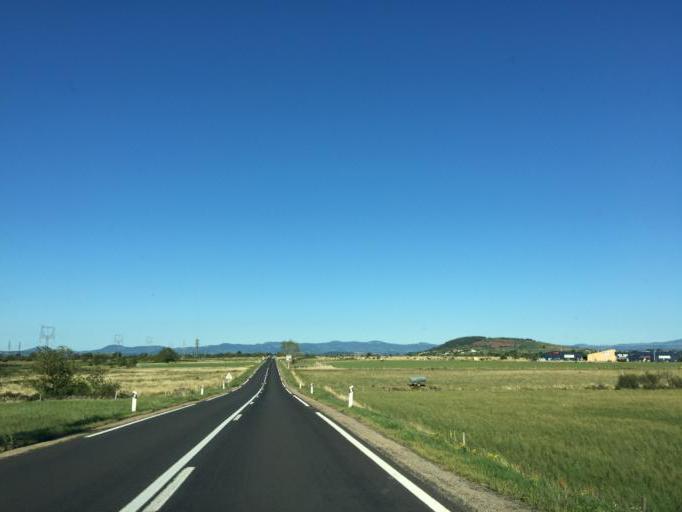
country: FR
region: Auvergne
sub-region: Departement de la Haute-Loire
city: Bains
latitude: 45.0108
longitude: 3.8102
